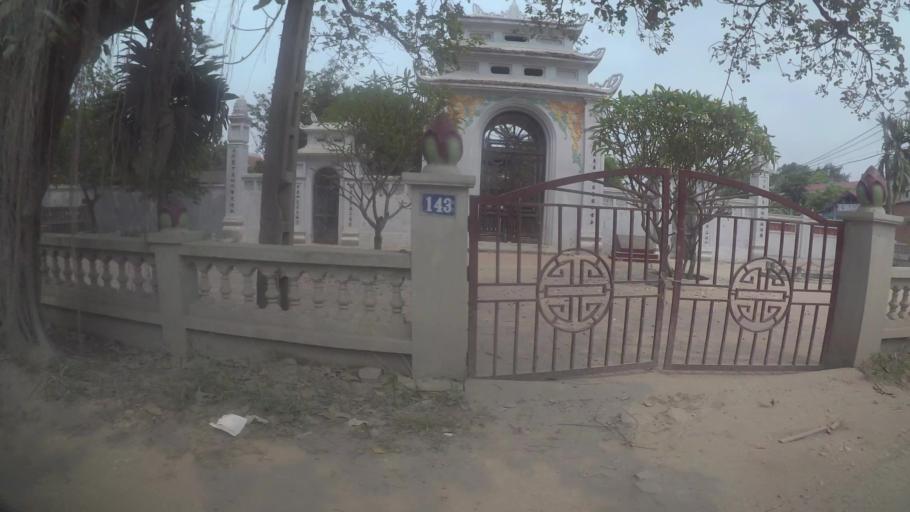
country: VN
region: Ha Noi
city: Cau Dien
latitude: 21.0366
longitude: 105.7380
